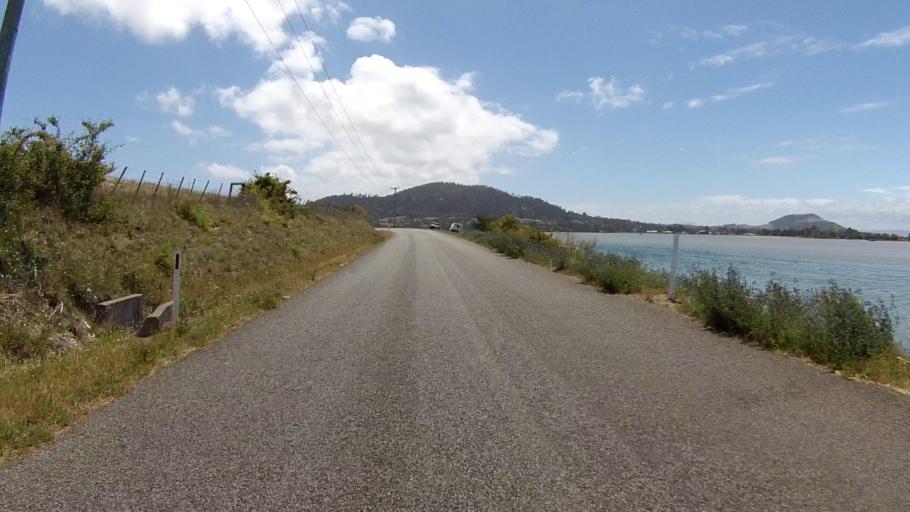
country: AU
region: Tasmania
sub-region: Clarence
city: Lauderdale
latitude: -42.9212
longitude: 147.4800
